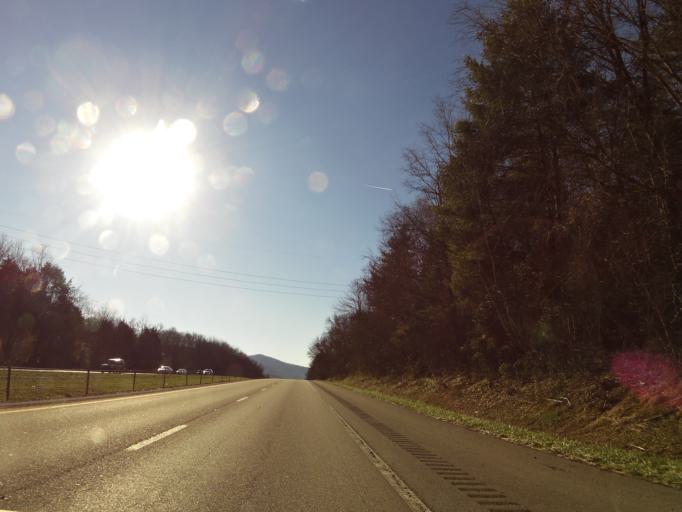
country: US
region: Tennessee
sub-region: Cocke County
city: Newport
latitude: 35.9188
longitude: -83.1882
